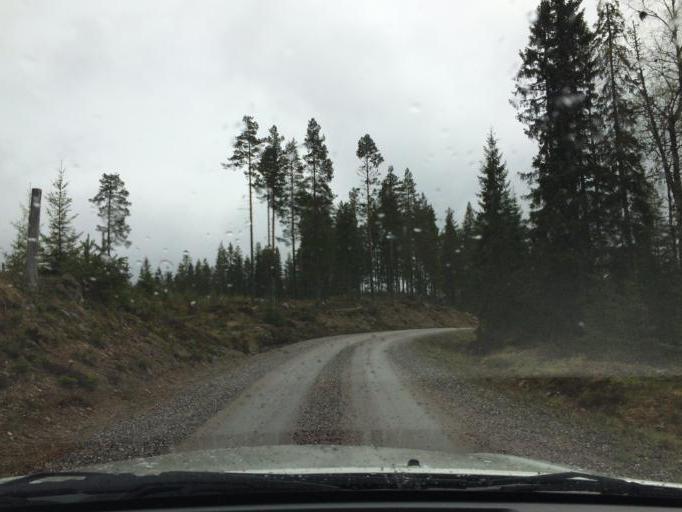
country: SE
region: OErebro
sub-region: Hallefors Kommun
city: Haellefors
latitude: 60.0179
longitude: 14.5873
